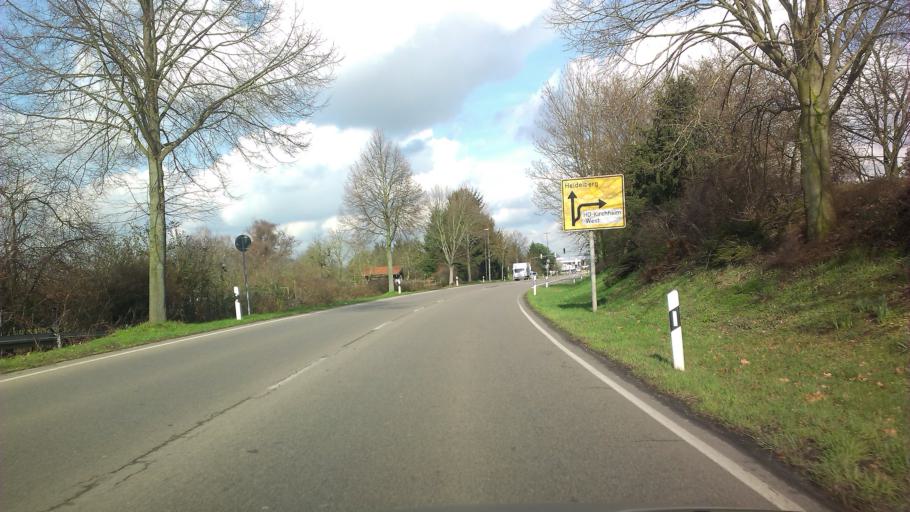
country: DE
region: Baden-Wuerttemberg
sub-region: Karlsruhe Region
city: Eppelheim
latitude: 49.3793
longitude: 8.6562
